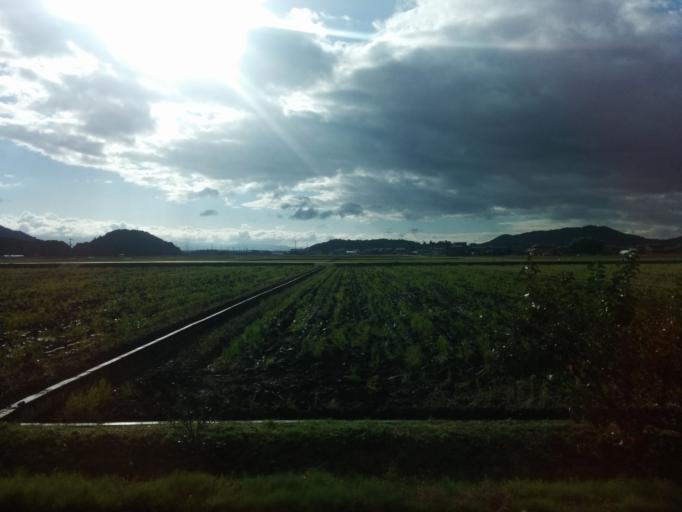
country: JP
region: Shiga Prefecture
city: Omihachiman
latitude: 35.1364
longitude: 136.1229
